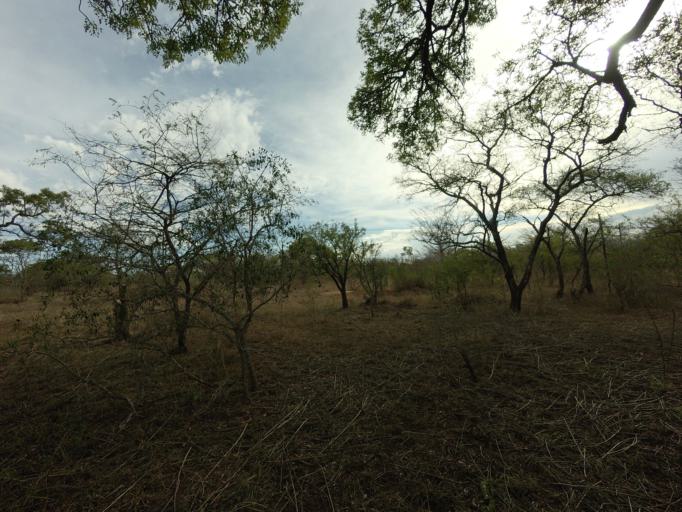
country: ZA
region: Limpopo
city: Thulamahashi
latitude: -24.5281
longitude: 31.1170
